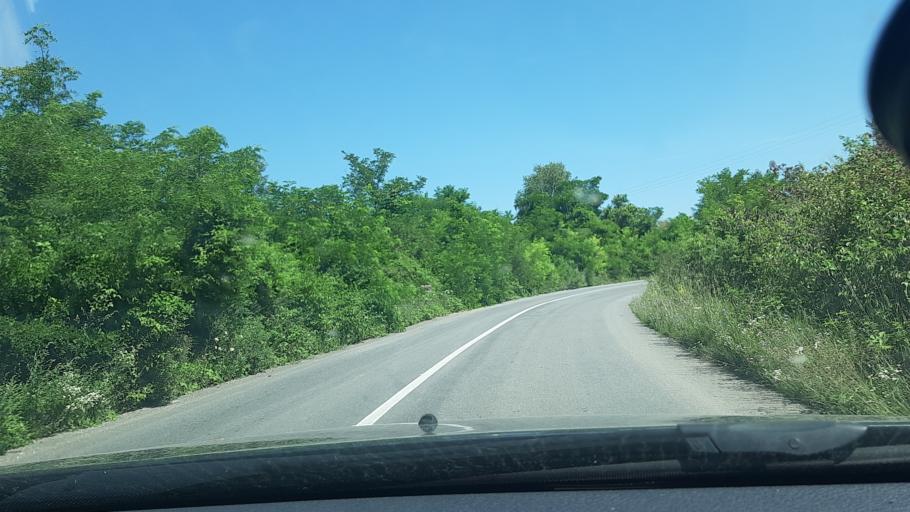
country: RO
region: Hunedoara
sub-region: Comuna Teliucu Inferior
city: Teliucu Inferior
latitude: 45.6953
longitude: 22.8754
